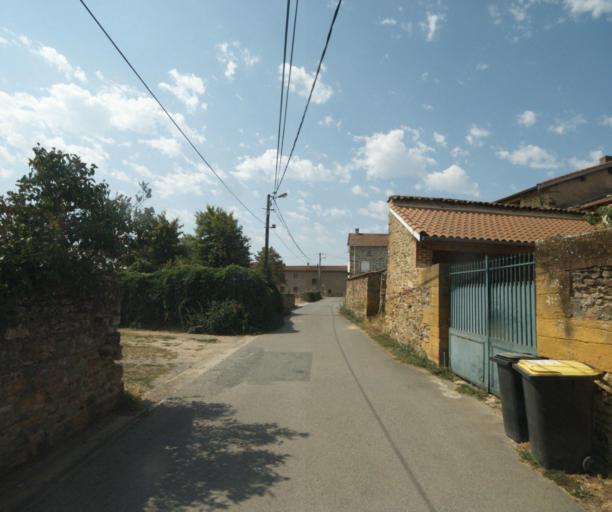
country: FR
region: Rhone-Alpes
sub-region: Departement du Rhone
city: Lentilly
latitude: 45.8360
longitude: 4.6572
